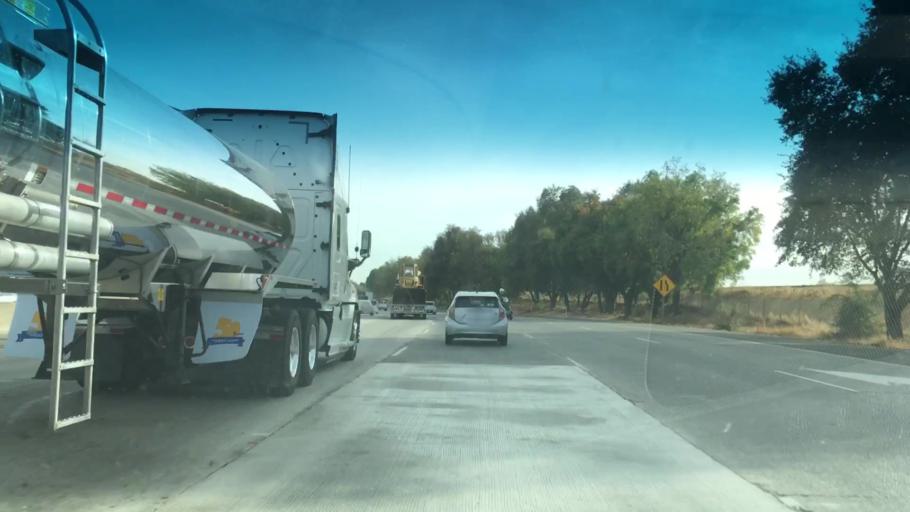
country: US
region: California
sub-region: Yolo County
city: West Sacramento
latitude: 38.5548
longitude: -121.5128
